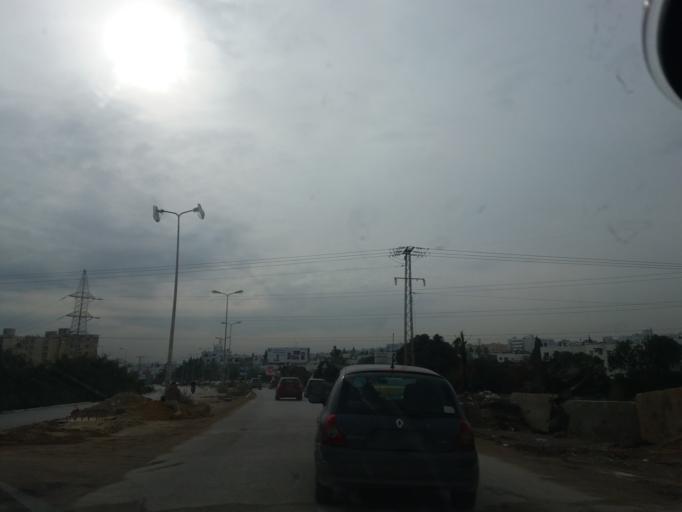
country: TN
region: Tunis
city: Tunis
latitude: 36.8521
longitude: 10.1533
